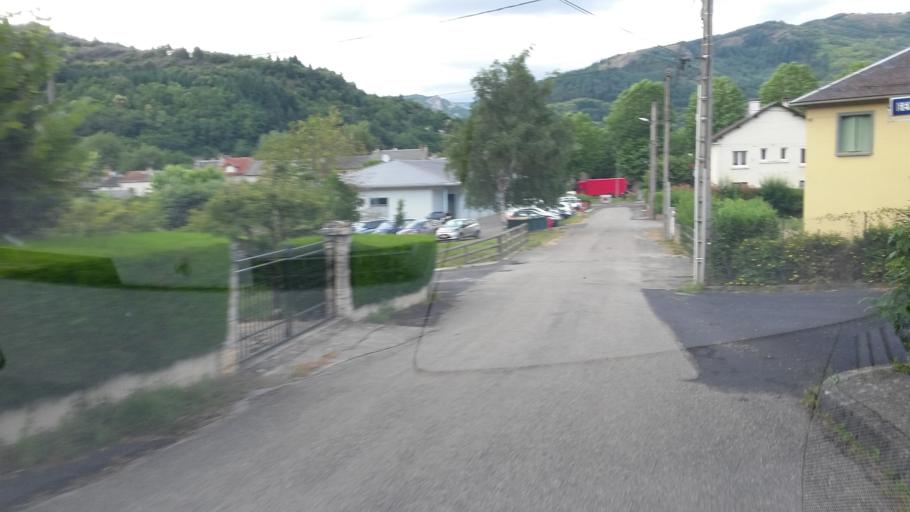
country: FR
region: Languedoc-Roussillon
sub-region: Departement de la Lozere
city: Meyrueis
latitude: 44.0205
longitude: 3.3603
